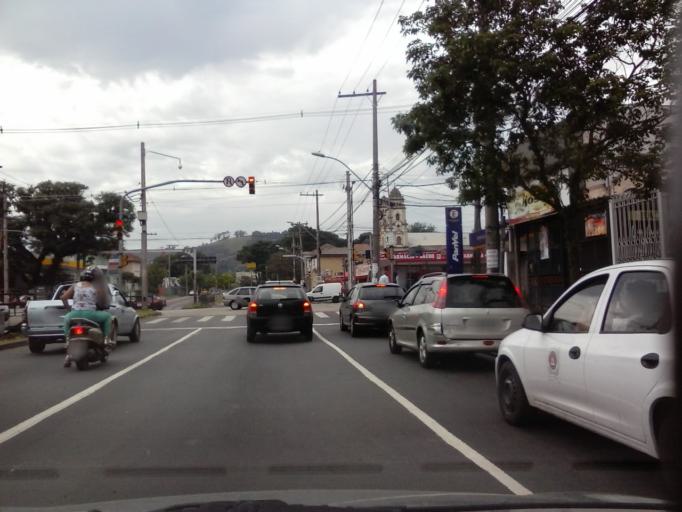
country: BR
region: Rio Grande do Sul
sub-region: Porto Alegre
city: Porto Alegre
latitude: -30.0737
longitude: -51.2030
